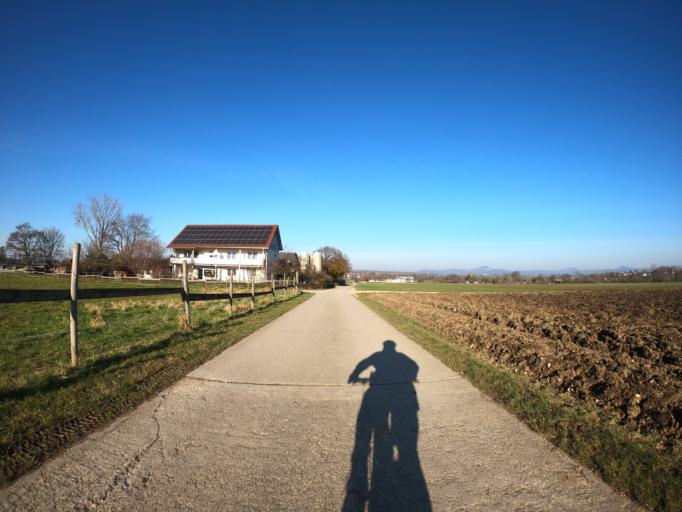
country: DE
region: Baden-Wuerttemberg
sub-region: Regierungsbezirk Stuttgart
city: Gammelshausen
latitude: 48.6499
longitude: 9.6521
